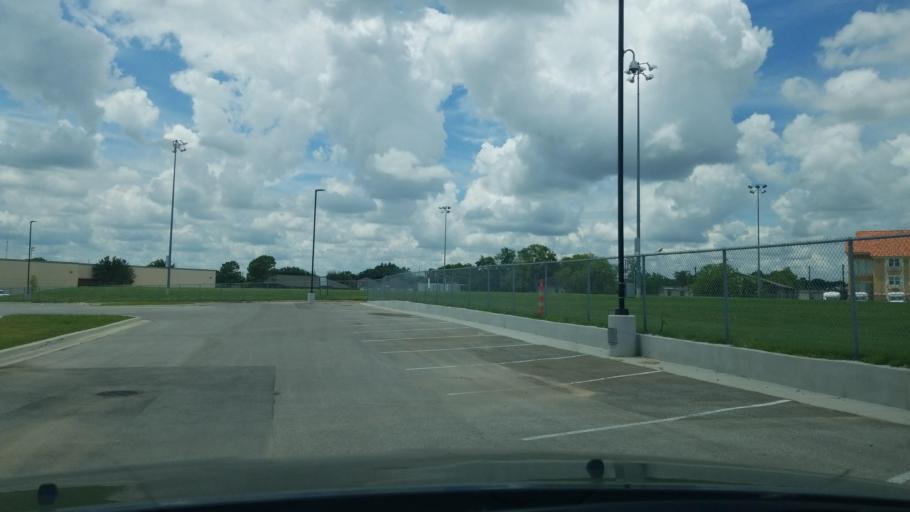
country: US
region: Texas
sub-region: Denton County
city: Denton
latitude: 33.2090
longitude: -97.1571
